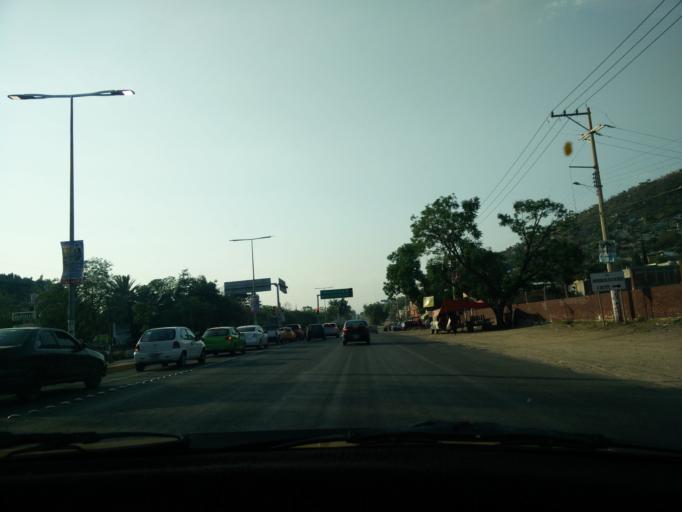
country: MX
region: Oaxaca
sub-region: Santa Maria Atzompa
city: San Jeronimo Yahuiche
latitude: 17.1029
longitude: -96.7523
